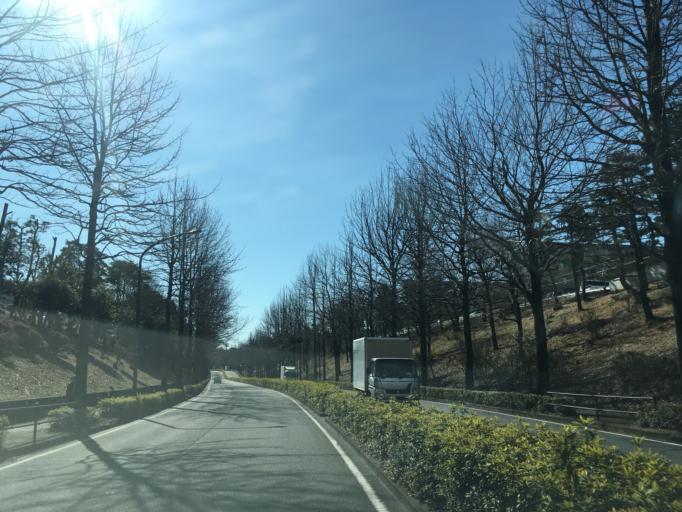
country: JP
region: Tokyo
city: Hino
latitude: 35.6145
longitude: 139.4322
